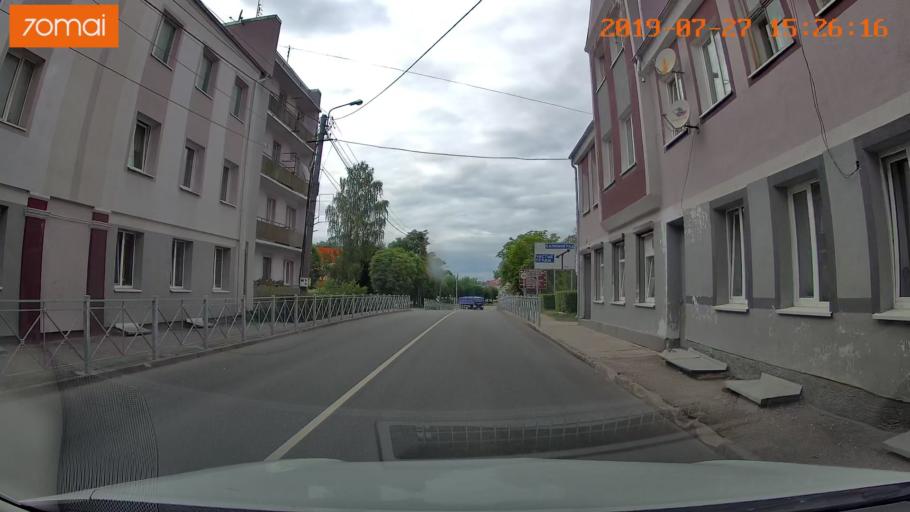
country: RU
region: Kaliningrad
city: Nesterov
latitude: 54.6310
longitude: 22.5745
